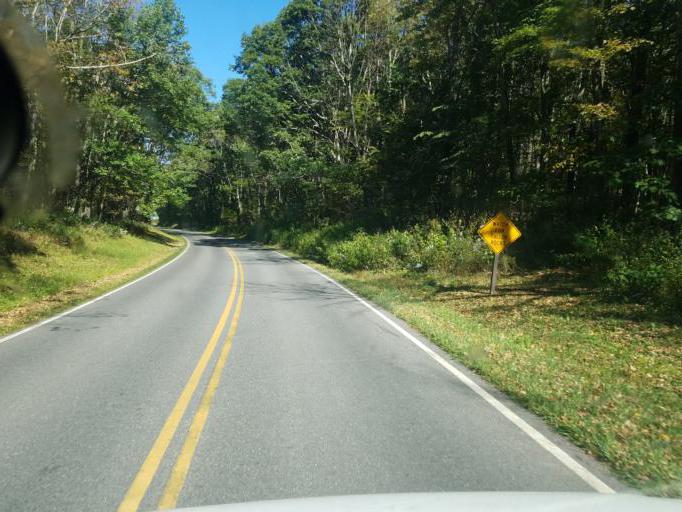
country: US
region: Virginia
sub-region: Greene County
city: Stanardsville
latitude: 38.4170
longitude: -78.4875
